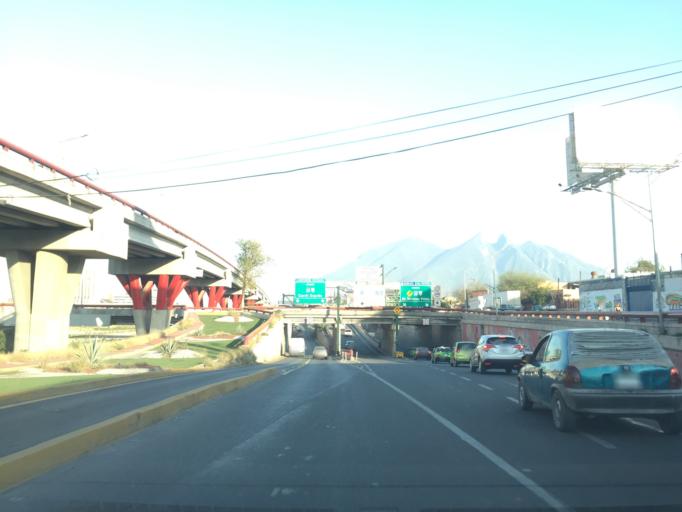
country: MX
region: Nuevo Leon
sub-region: Monterrey
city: Monterrey
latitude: 25.6637
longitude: -100.3221
